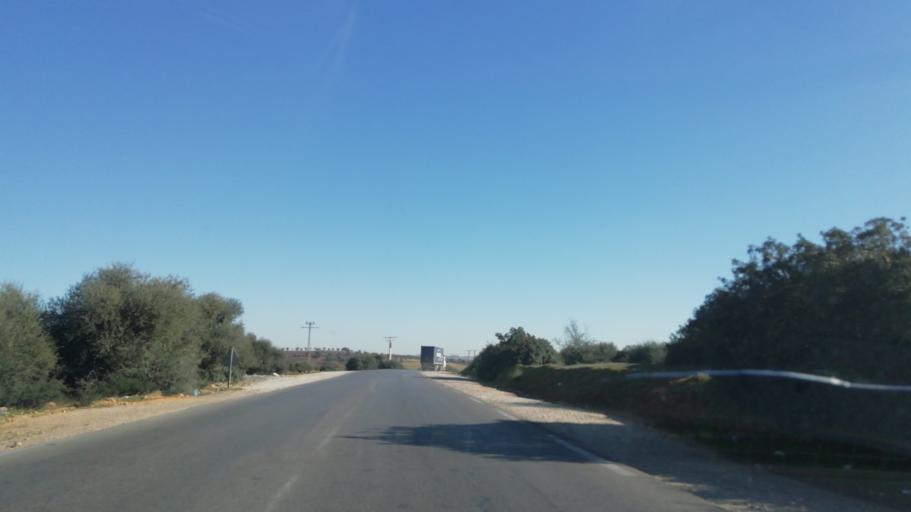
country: DZ
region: Relizane
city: Smala
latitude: 35.6904
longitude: 0.7927
